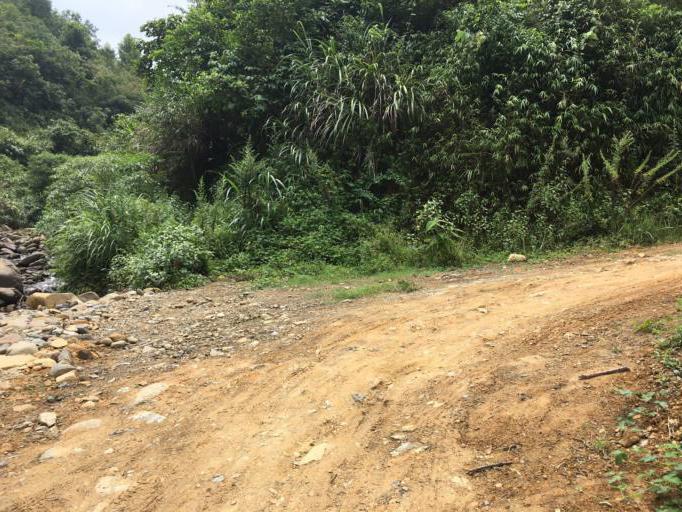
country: CN
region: Guangxi Zhuangzu Zizhiqu
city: Tongle
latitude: 25.2977
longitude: 106.1438
